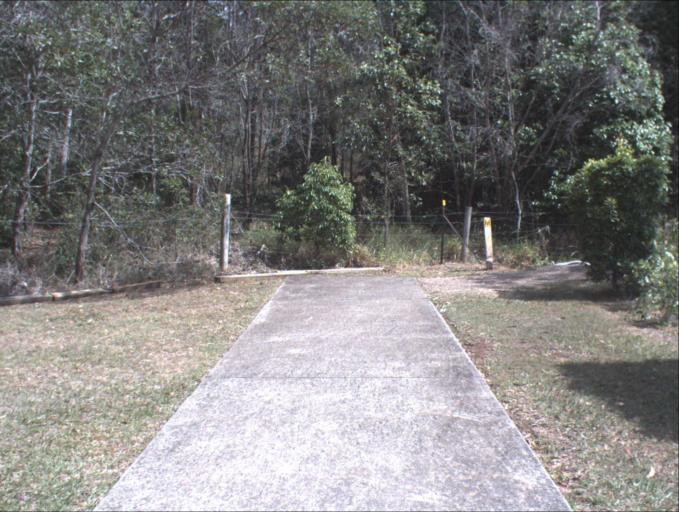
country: AU
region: Queensland
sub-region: Logan
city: Woodridge
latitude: -27.6145
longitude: 153.1065
